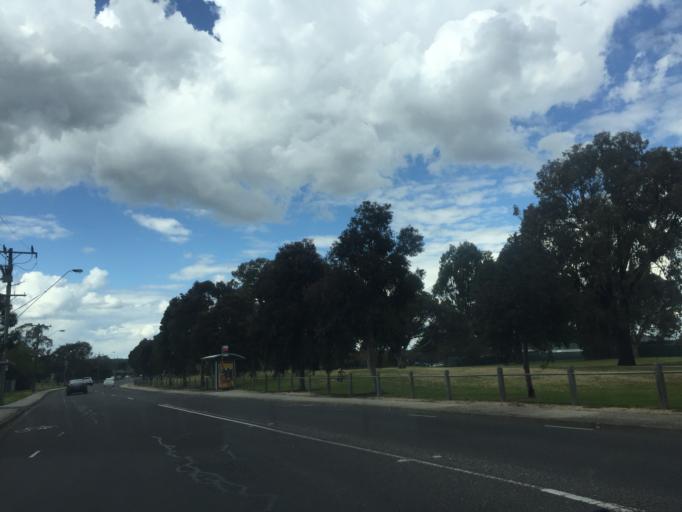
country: AU
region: Victoria
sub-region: Darebin
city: Kingsbury
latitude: -37.7150
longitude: 145.0223
